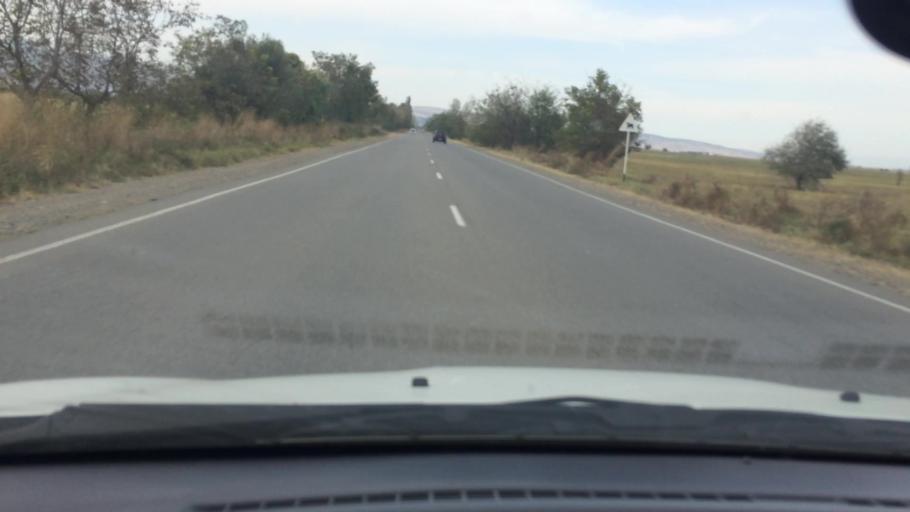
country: GE
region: Kvemo Kartli
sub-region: Marneuli
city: Marneuli
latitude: 41.5475
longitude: 44.7765
